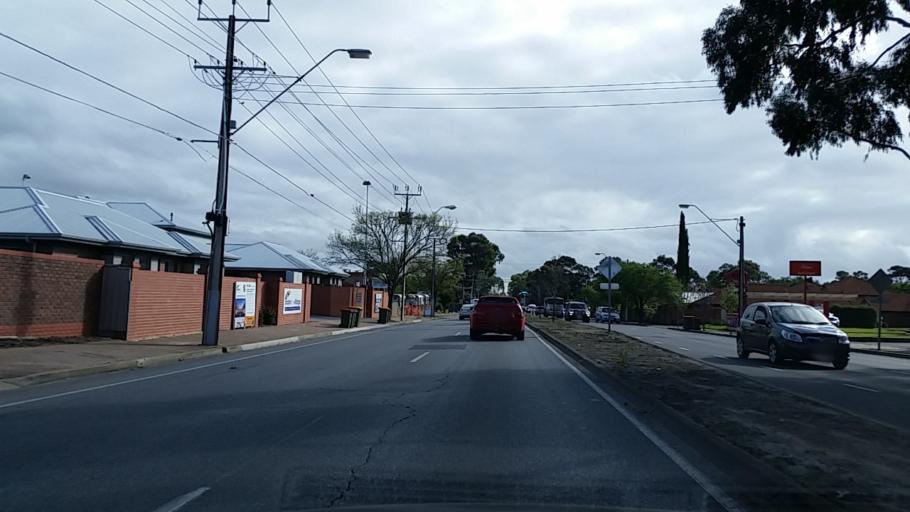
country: AU
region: South Australia
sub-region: Norwood Payneham St Peters
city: Payneham
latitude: -34.8930
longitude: 138.6477
